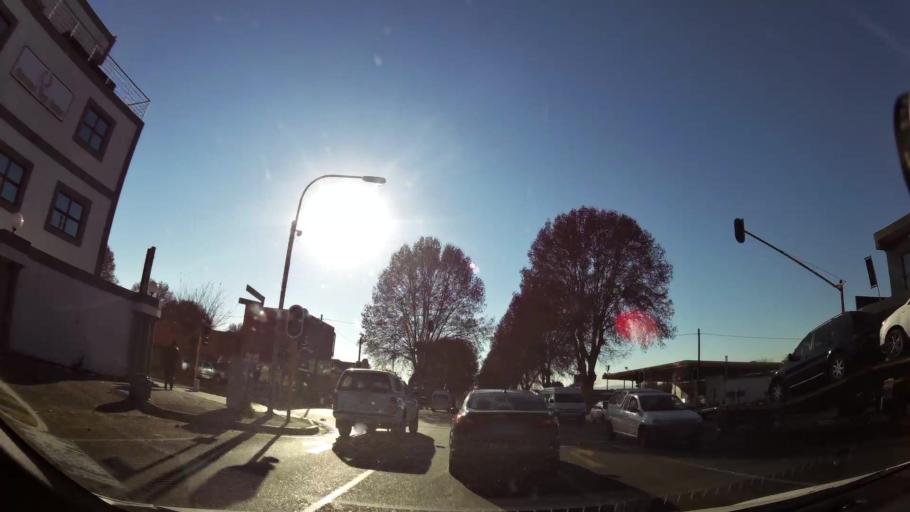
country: ZA
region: Gauteng
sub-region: City of Johannesburg Metropolitan Municipality
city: Johannesburg
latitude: -26.1885
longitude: 28.0929
